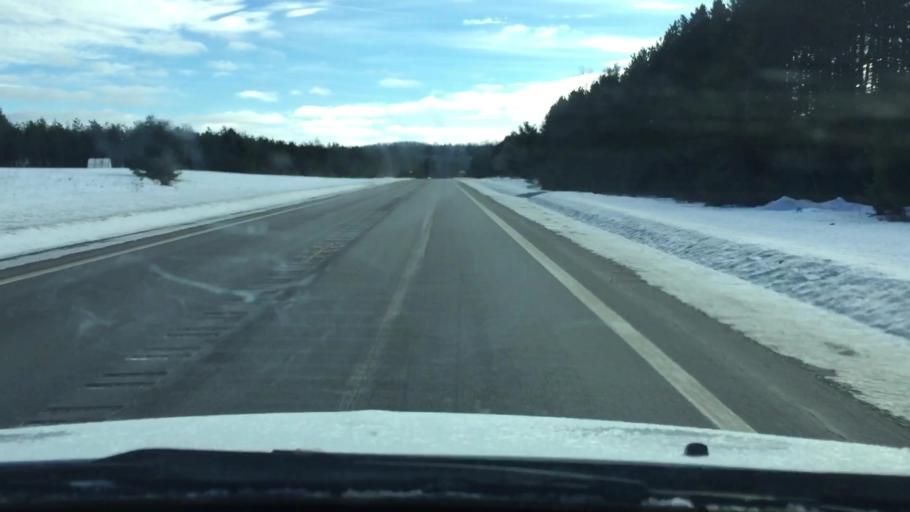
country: US
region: Michigan
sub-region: Antrim County
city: Mancelona
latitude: 44.9642
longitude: -85.0525
